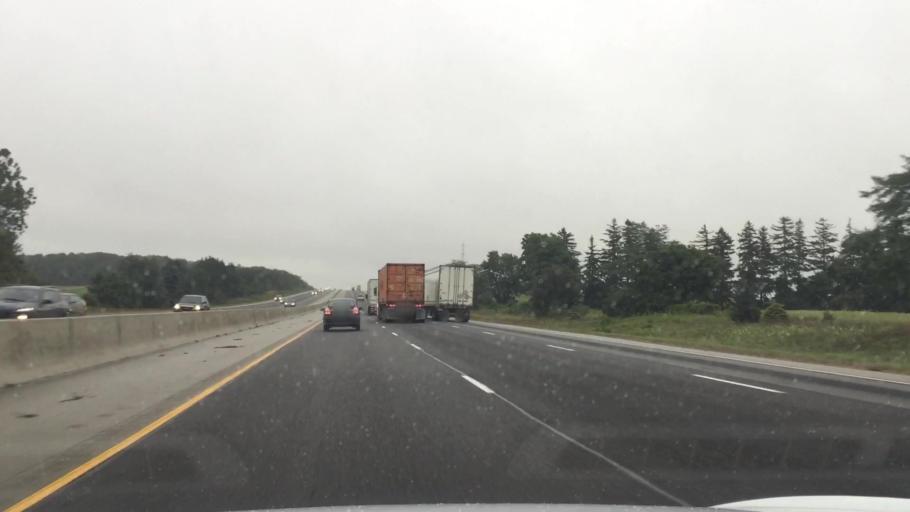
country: CA
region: Ontario
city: Kitchener
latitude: 43.2827
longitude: -80.5162
